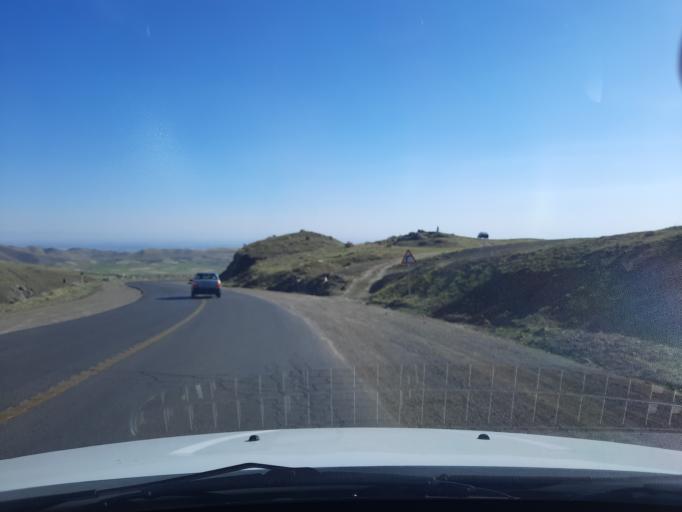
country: IR
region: Qazvin
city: Qazvin
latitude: 36.3665
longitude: 50.2005
